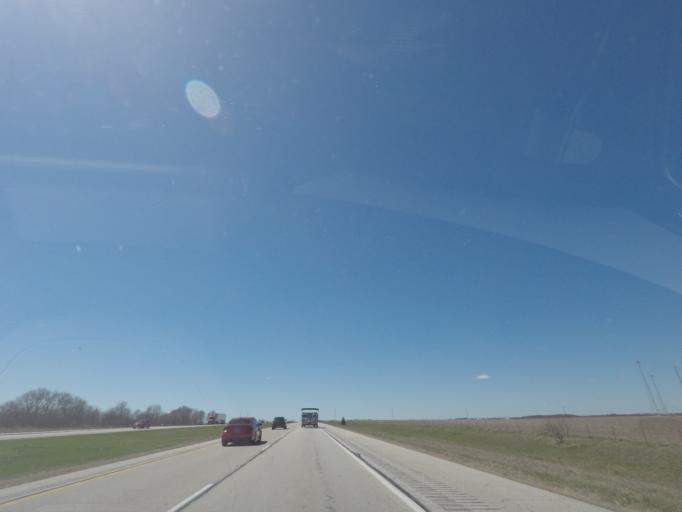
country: US
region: Illinois
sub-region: McLean County
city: Lexington
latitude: 40.5966
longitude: -88.8514
